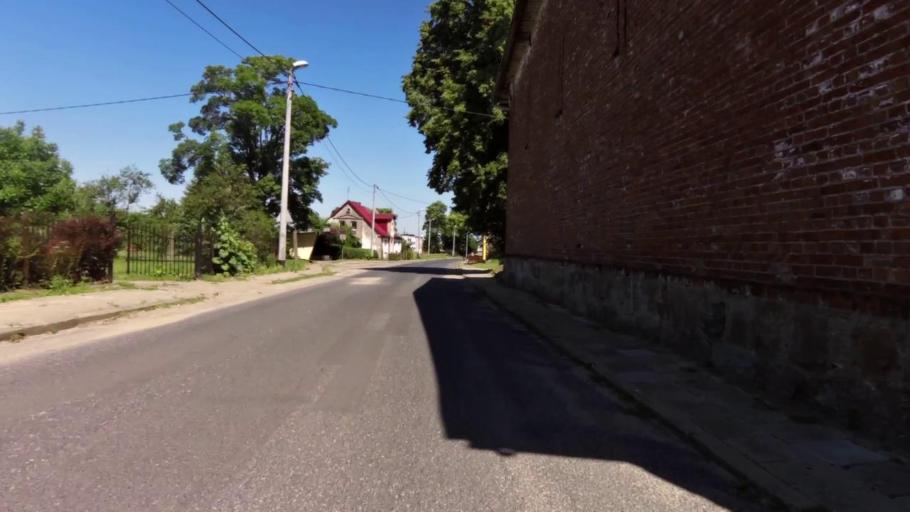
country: PL
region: West Pomeranian Voivodeship
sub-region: Powiat swidwinski
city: Rabino
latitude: 53.8421
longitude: 15.9976
